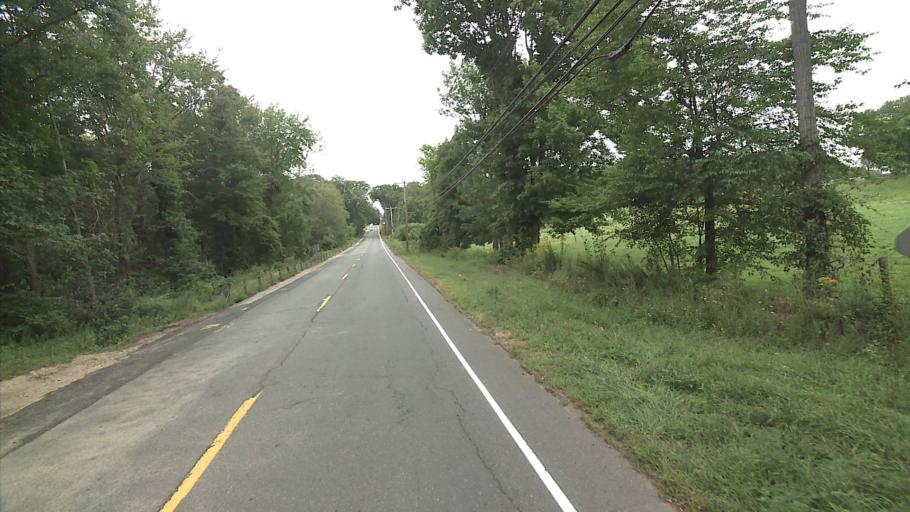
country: US
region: Connecticut
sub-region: Hartford County
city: Manchester
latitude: 41.7722
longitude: -72.4517
